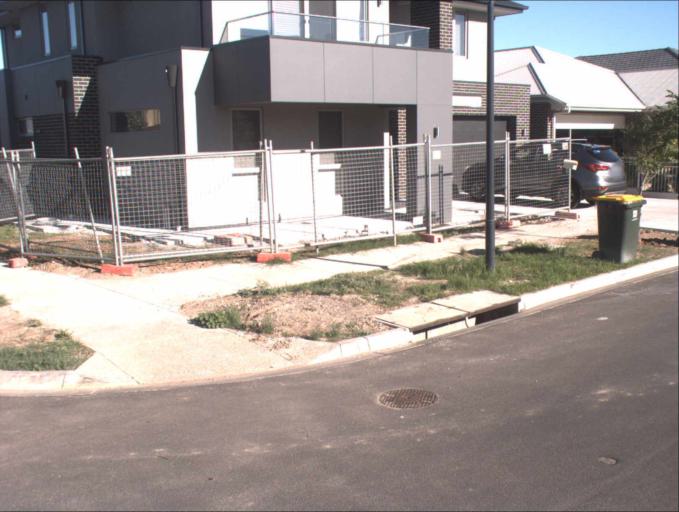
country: AU
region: South Australia
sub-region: Port Adelaide Enfield
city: Klemzig
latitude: -34.8611
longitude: 138.6288
